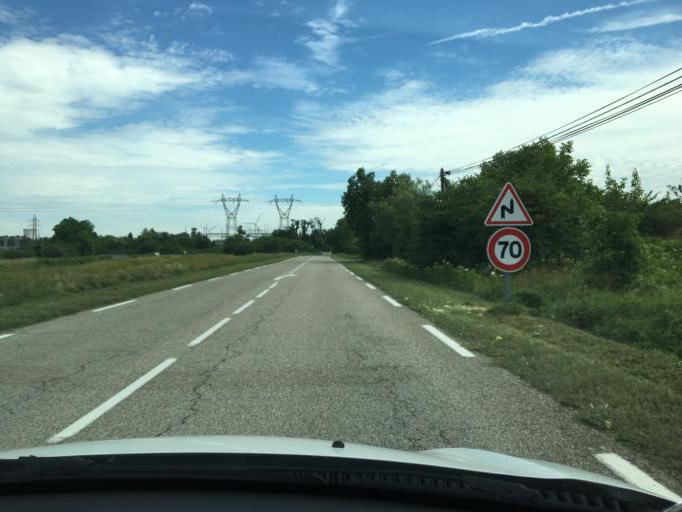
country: FR
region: Provence-Alpes-Cote d'Azur
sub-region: Departement du Vaucluse
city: Bollene
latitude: 44.2983
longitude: 4.7347
